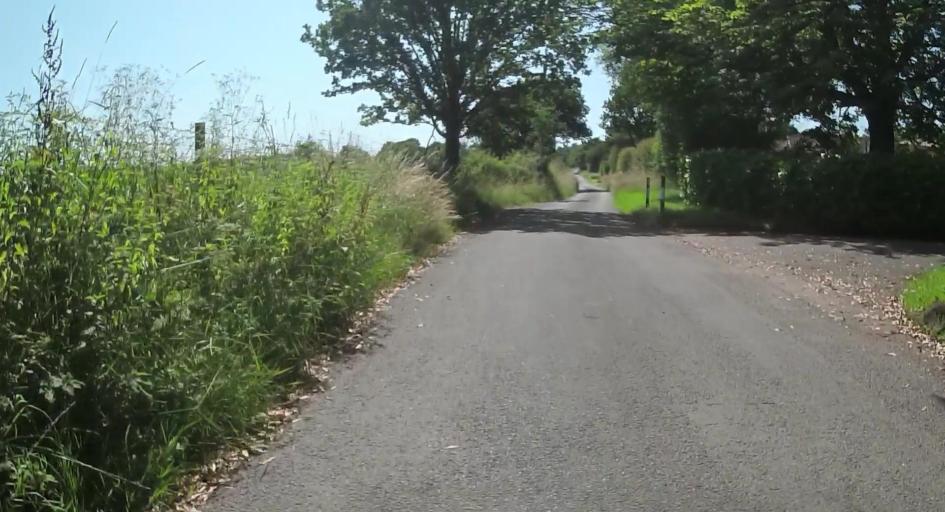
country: GB
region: England
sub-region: Hampshire
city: Lindford
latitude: 51.1516
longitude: -0.8189
